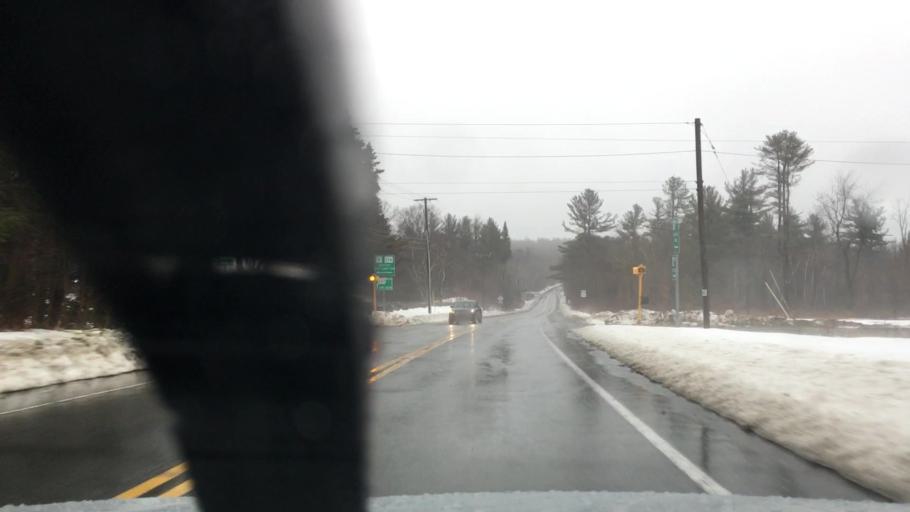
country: US
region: Massachusetts
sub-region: Hampshire County
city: Pelham
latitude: 42.3919
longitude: -72.4034
